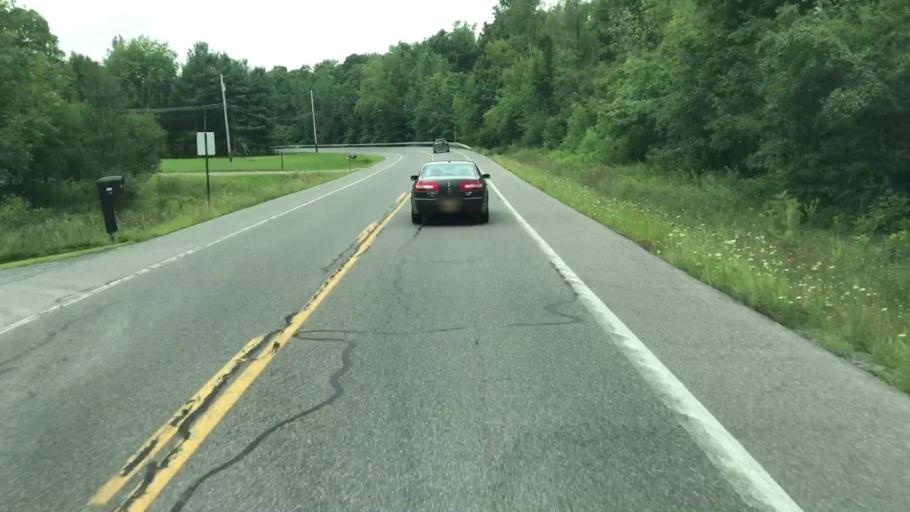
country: US
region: New York
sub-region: Onondaga County
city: Camillus
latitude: 43.0711
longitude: -76.3251
